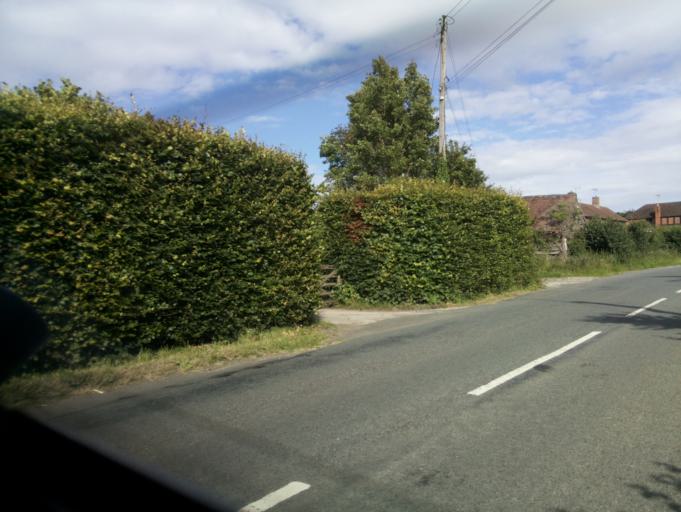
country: GB
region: England
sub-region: Gloucestershire
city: Stonehouse
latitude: 51.7923
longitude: -2.2725
